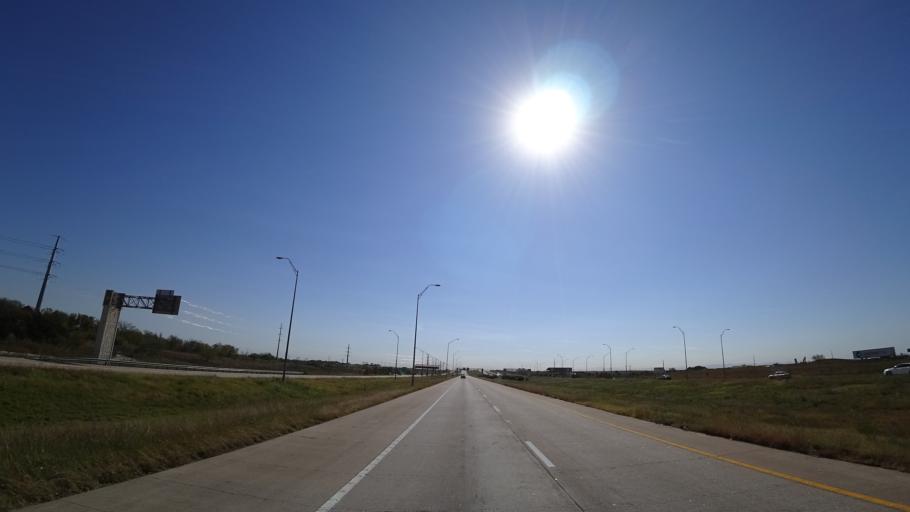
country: US
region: Texas
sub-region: Travis County
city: Pflugerville
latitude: 30.4174
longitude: -97.5861
